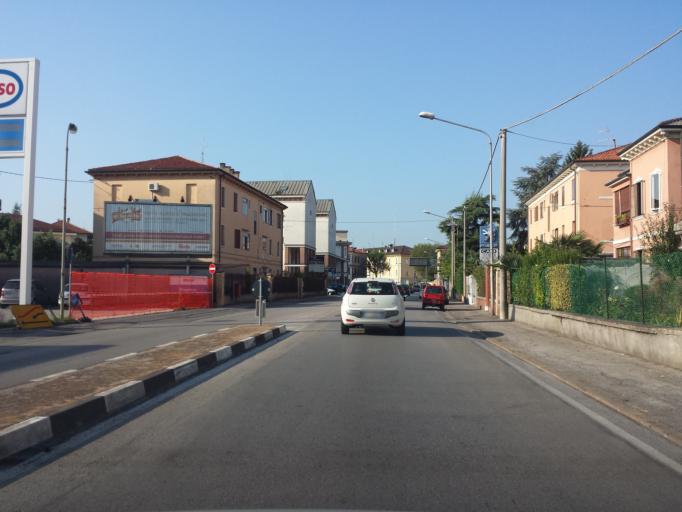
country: IT
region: Veneto
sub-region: Provincia di Vicenza
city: Vicenza
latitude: 45.5633
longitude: 11.5458
